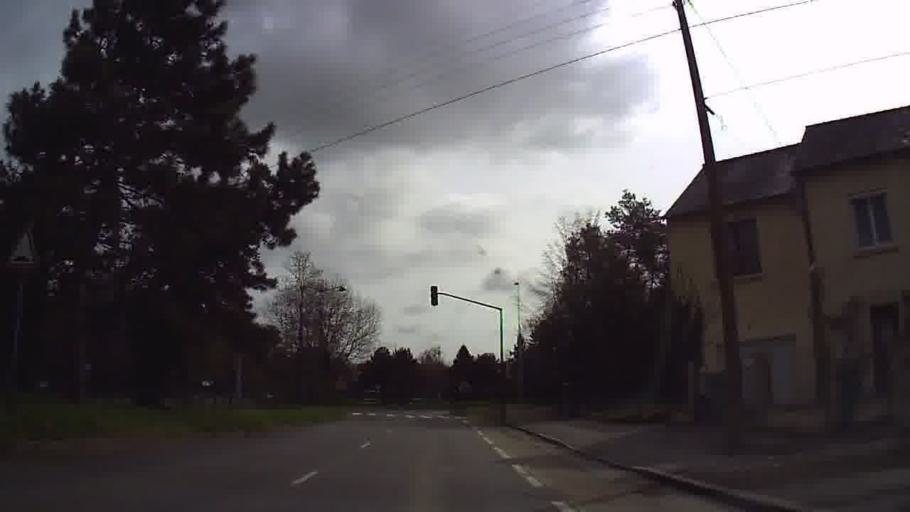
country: FR
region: Brittany
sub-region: Departement d'Ille-et-Vilaine
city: Rennes
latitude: 48.1276
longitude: -1.6535
